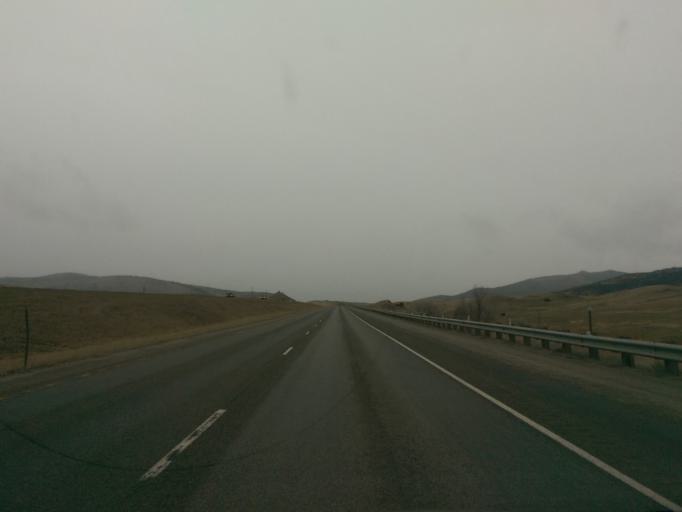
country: US
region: Montana
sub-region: Gallatin County
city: Three Forks
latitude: 45.9043
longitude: -111.8060
